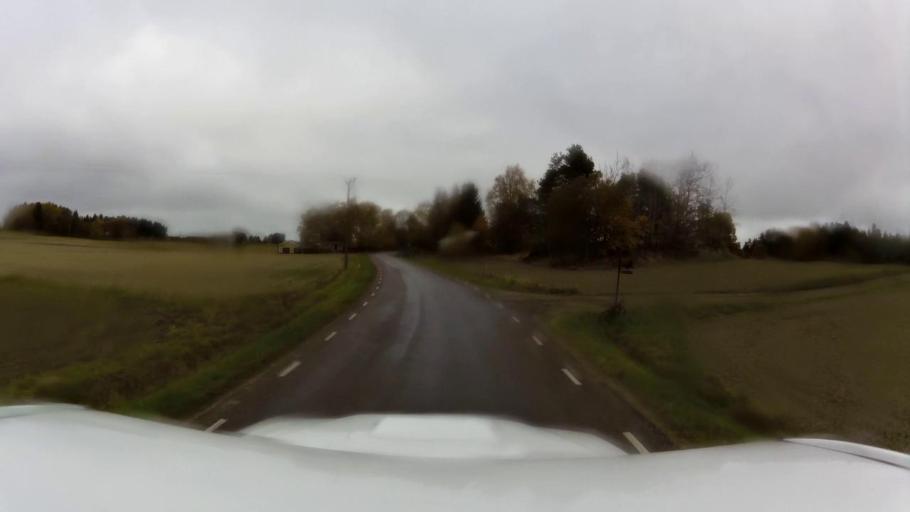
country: SE
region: OEstergoetland
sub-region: Linkopings Kommun
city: Linghem
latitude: 58.4594
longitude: 15.8289
